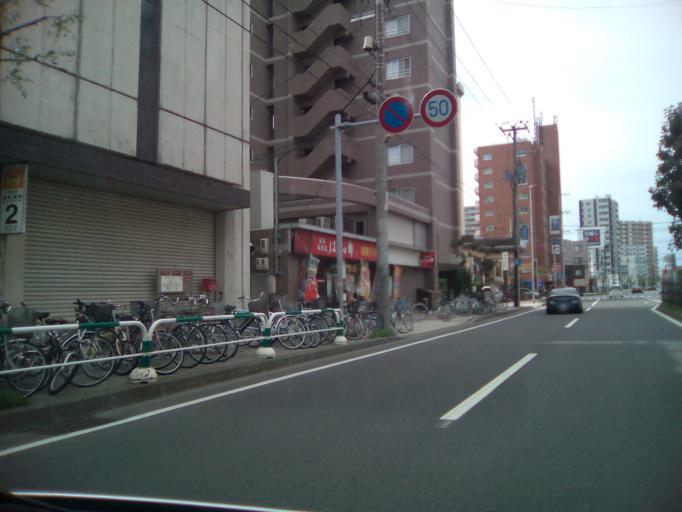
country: JP
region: Hokkaido
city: Sapporo
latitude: 43.0518
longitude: 141.3849
